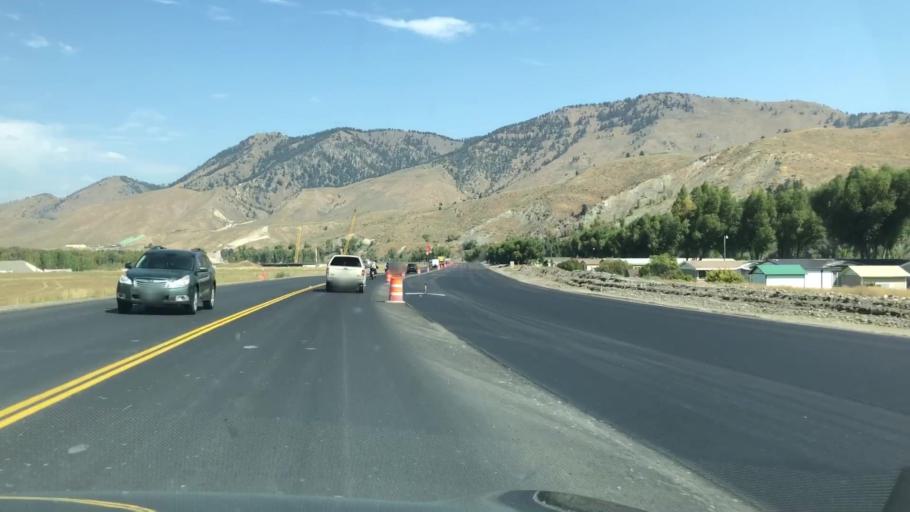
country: US
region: Wyoming
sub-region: Teton County
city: South Park
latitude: 43.3766
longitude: -110.7450
